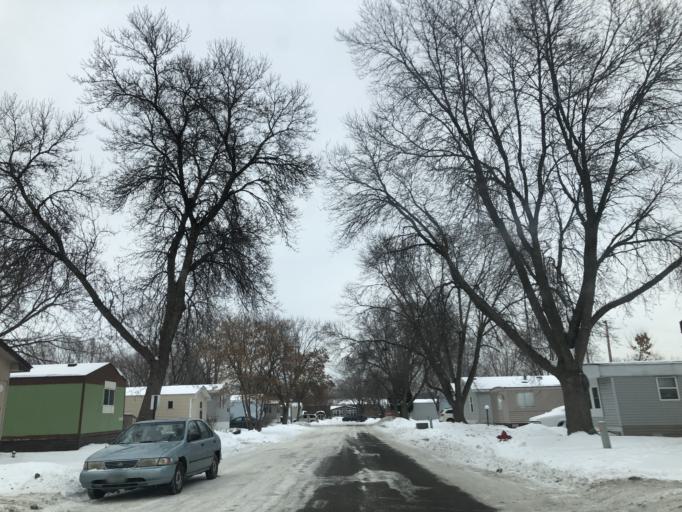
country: US
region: Minnesota
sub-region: Ramsey County
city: New Brighton
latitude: 45.0797
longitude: -93.1816
